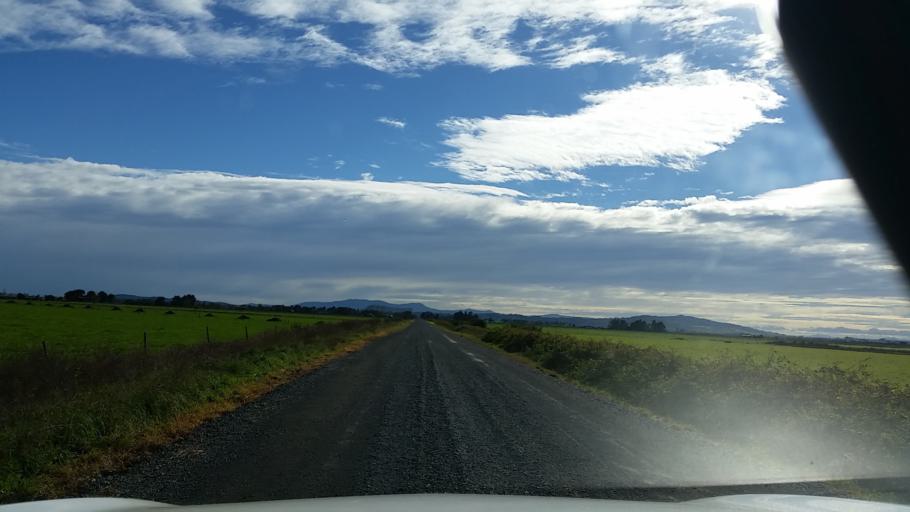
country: NZ
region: Waikato
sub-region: Hamilton City
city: Hamilton
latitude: -37.6825
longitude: 175.4439
